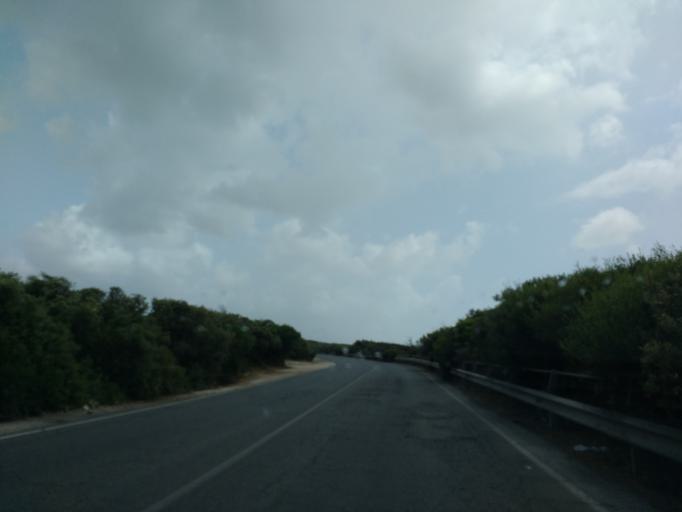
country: IT
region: Latium
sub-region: Citta metropolitana di Roma Capitale
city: Torvaianica
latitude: 41.6695
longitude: 12.3994
